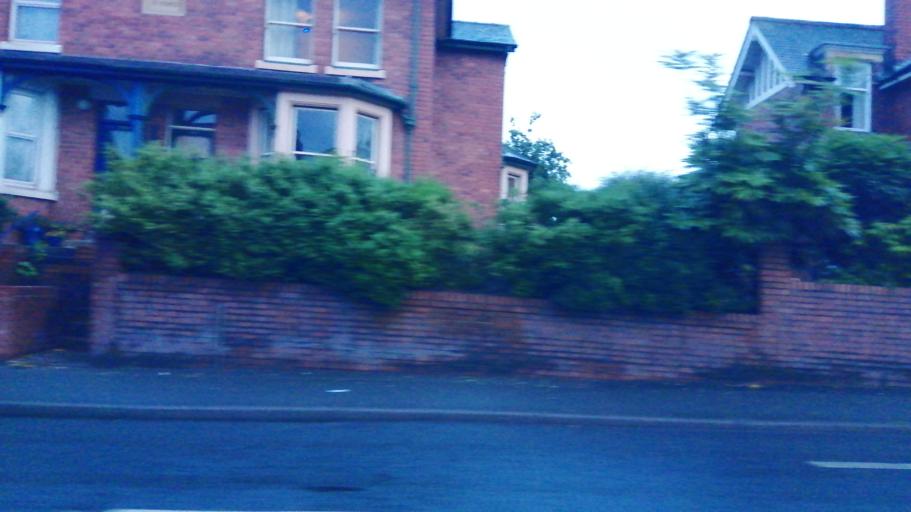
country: GB
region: England
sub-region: Herefordshire
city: Belmont
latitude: 52.0456
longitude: -2.7266
